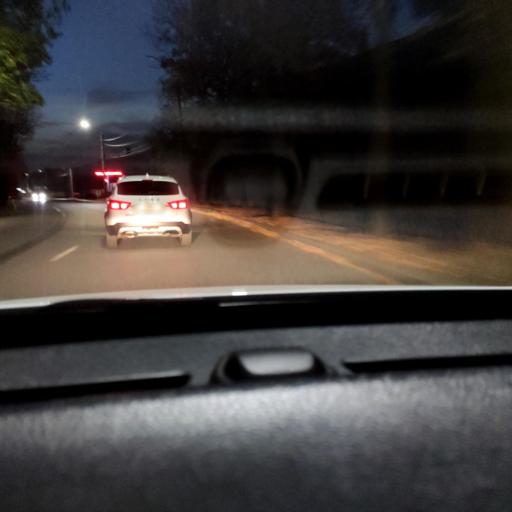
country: RU
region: Voronezj
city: Voronezh
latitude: 51.6864
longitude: 39.1773
